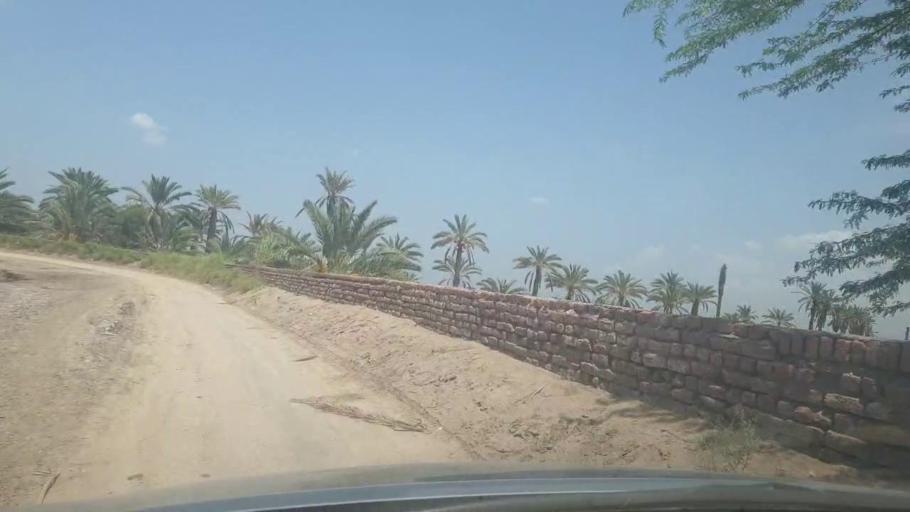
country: PK
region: Sindh
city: Kot Diji
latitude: 27.3862
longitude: 68.6976
